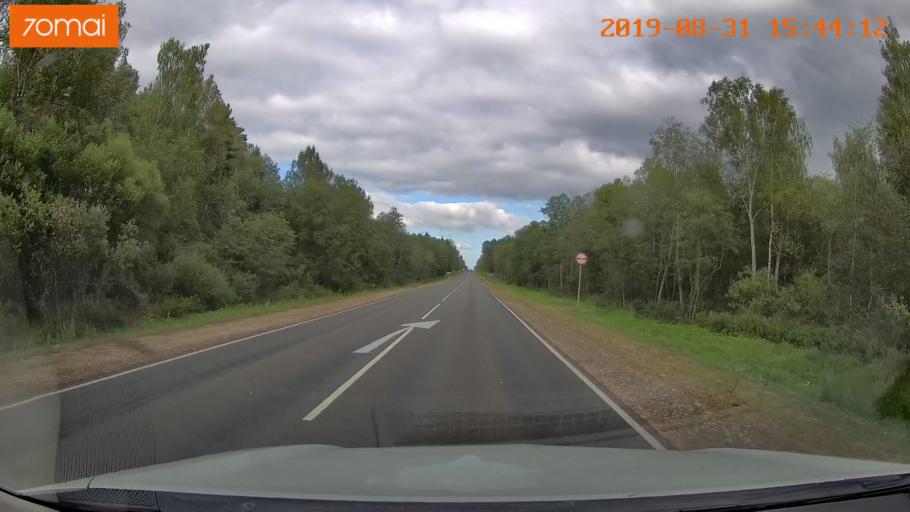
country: RU
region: Kaluga
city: Mosal'sk
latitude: 54.6575
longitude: 34.9271
